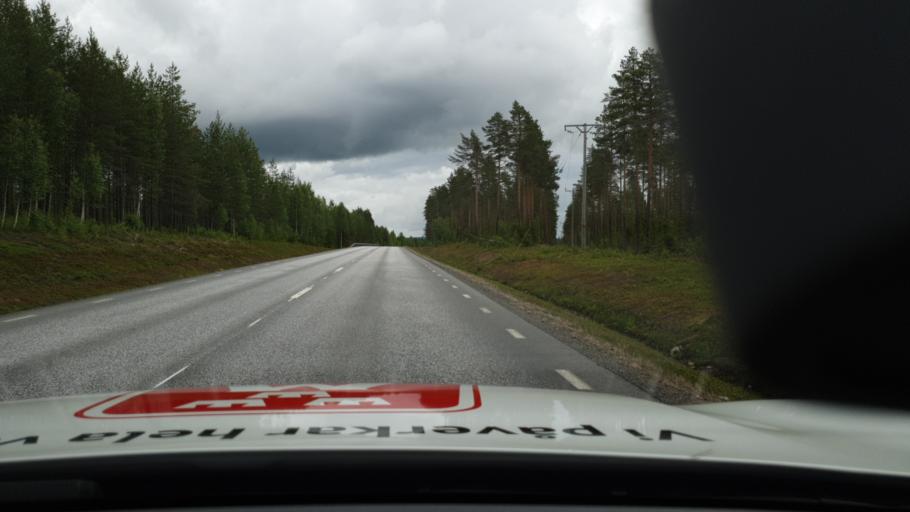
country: SE
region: Norrbotten
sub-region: Pitea Kommun
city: Rosvik
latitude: 65.5966
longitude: 21.6146
